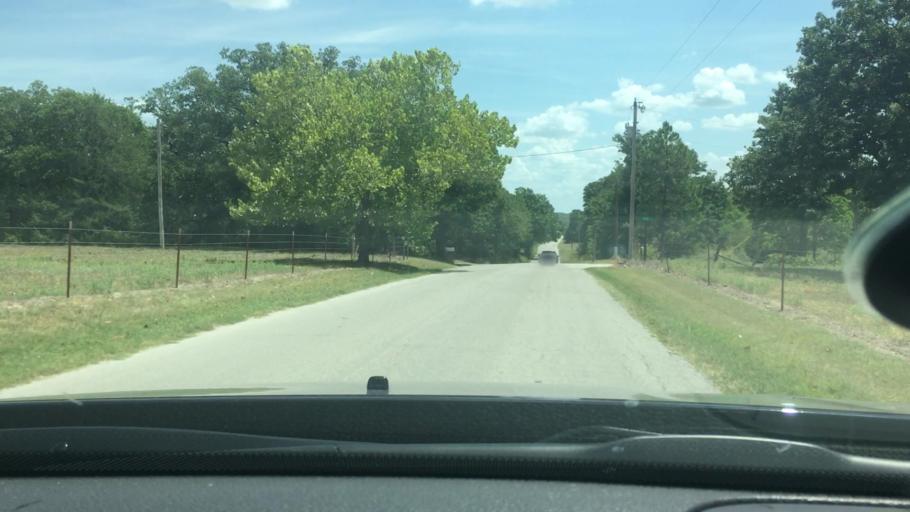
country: US
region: Oklahoma
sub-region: Carter County
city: Ardmore
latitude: 34.0710
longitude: -97.1920
